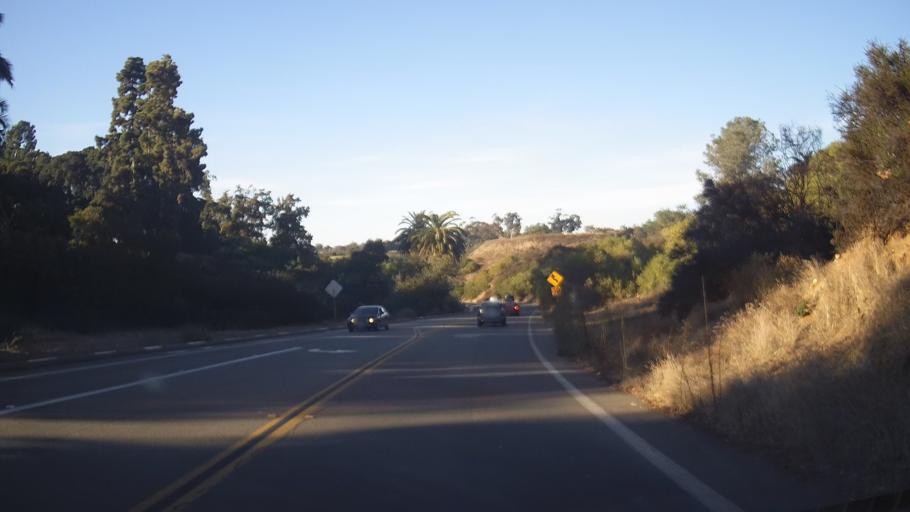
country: US
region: California
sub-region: San Diego County
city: San Diego
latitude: 32.7202
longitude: -117.1384
